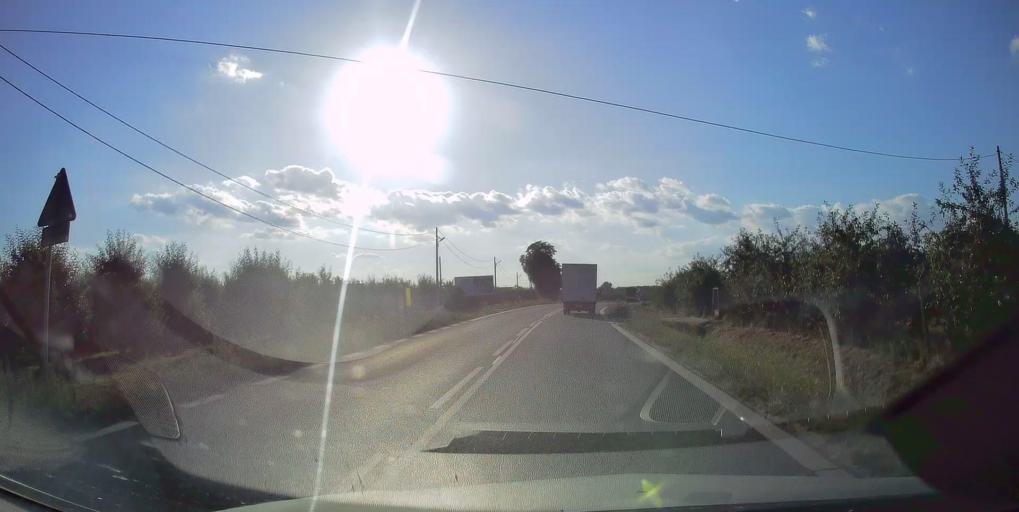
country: PL
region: Lodz Voivodeship
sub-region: Powiat rawski
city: Biala Rawska
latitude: 51.8029
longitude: 20.5057
